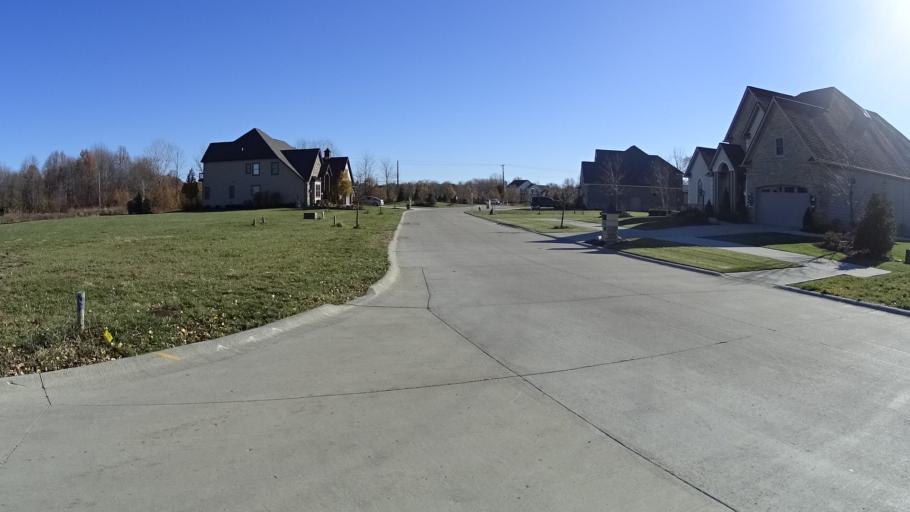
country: US
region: Ohio
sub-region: Lorain County
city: North Ridgeville
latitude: 41.4213
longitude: -81.9913
